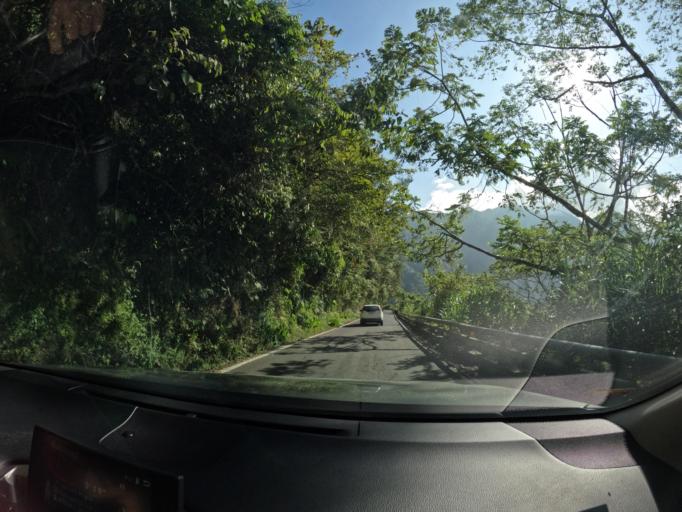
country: TW
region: Taiwan
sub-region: Taitung
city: Taitung
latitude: 23.1969
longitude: 121.0183
